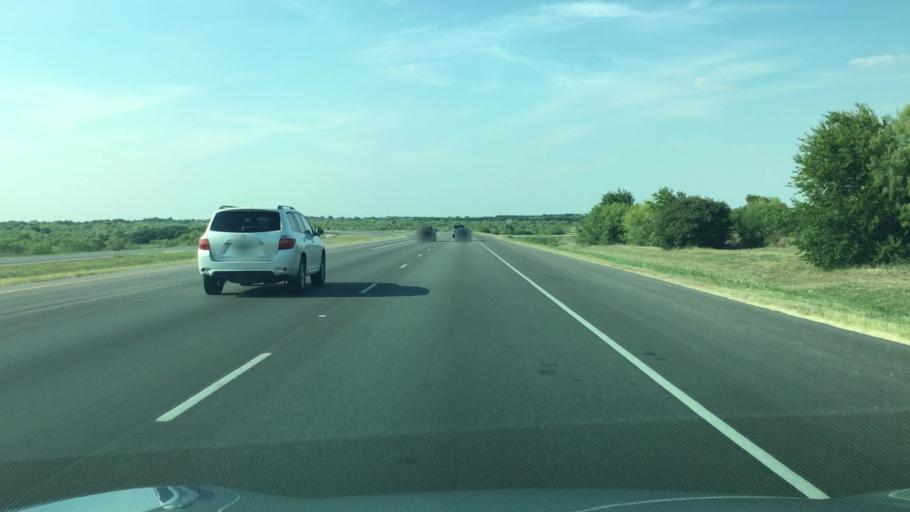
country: US
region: Texas
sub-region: Hays County
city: Kyle
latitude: 30.0330
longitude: -97.8723
